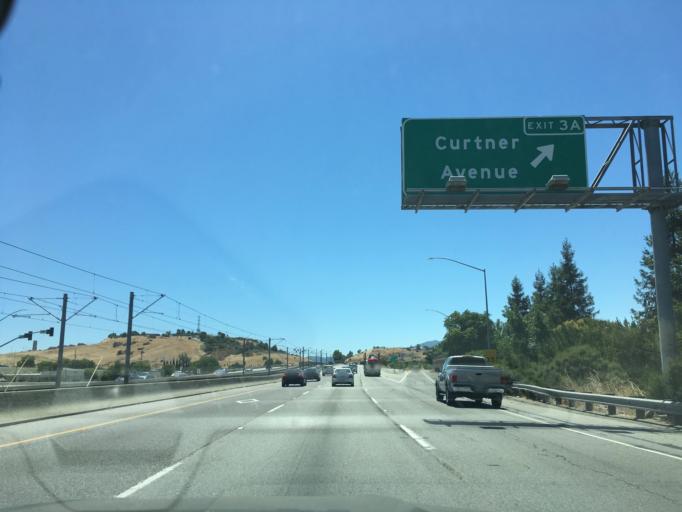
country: US
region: California
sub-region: Santa Clara County
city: Seven Trees
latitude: 37.2984
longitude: -121.8748
